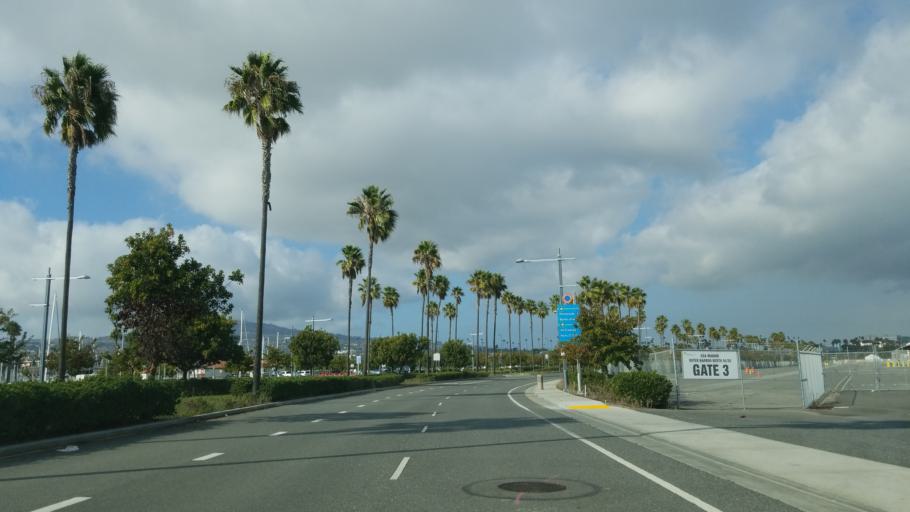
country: US
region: California
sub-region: Los Angeles County
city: San Pedro
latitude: 33.7218
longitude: -118.2759
